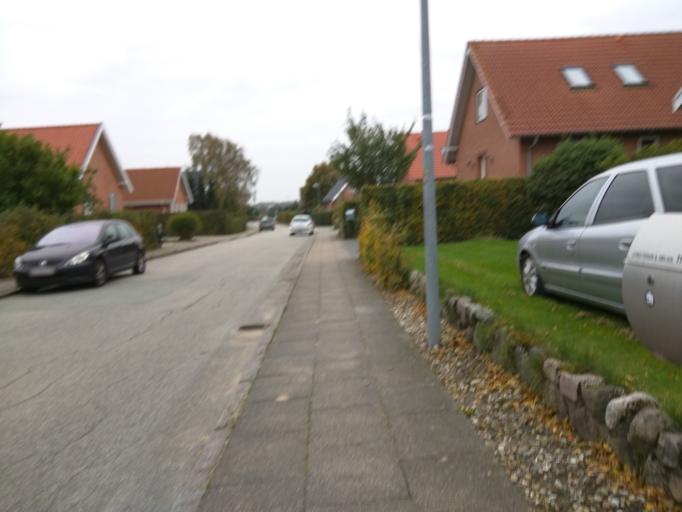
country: DK
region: Central Jutland
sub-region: Viborg Kommune
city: Viborg
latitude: 56.4558
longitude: 9.3880
